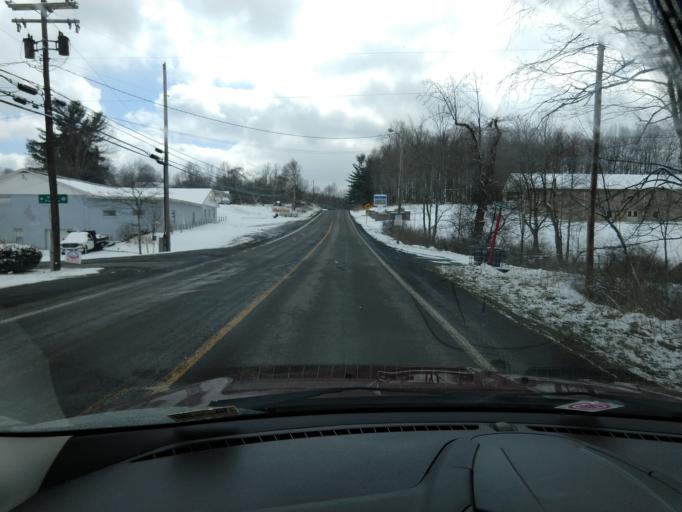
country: US
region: West Virginia
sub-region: Nicholas County
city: Craigsville
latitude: 38.3153
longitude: -80.6546
